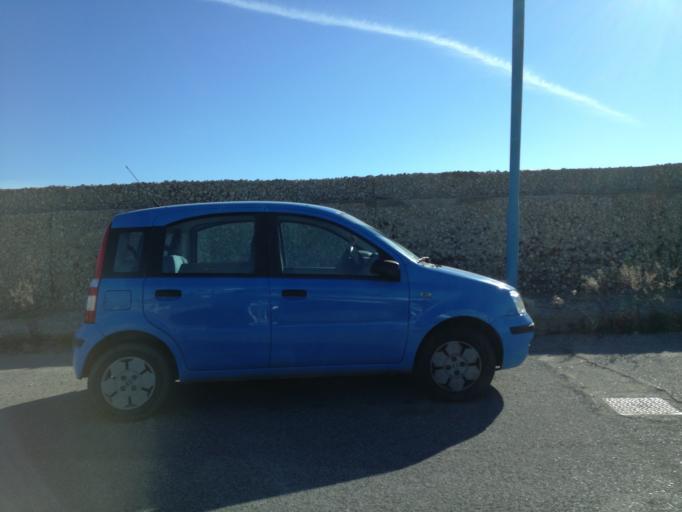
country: IT
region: Sicily
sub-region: Provincia di Caltanissetta
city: Gela
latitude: 37.0652
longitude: 14.2323
